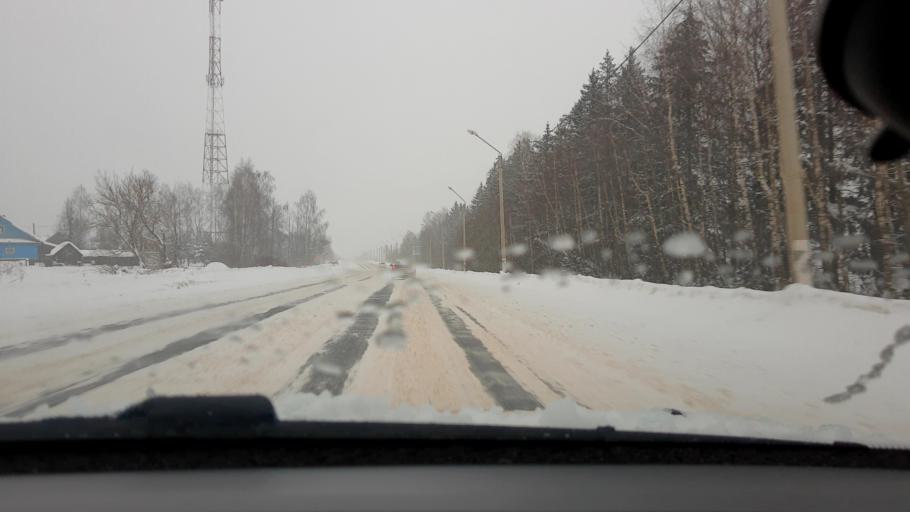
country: RU
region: Nizjnij Novgorod
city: Purekh
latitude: 56.6600
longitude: 43.0970
